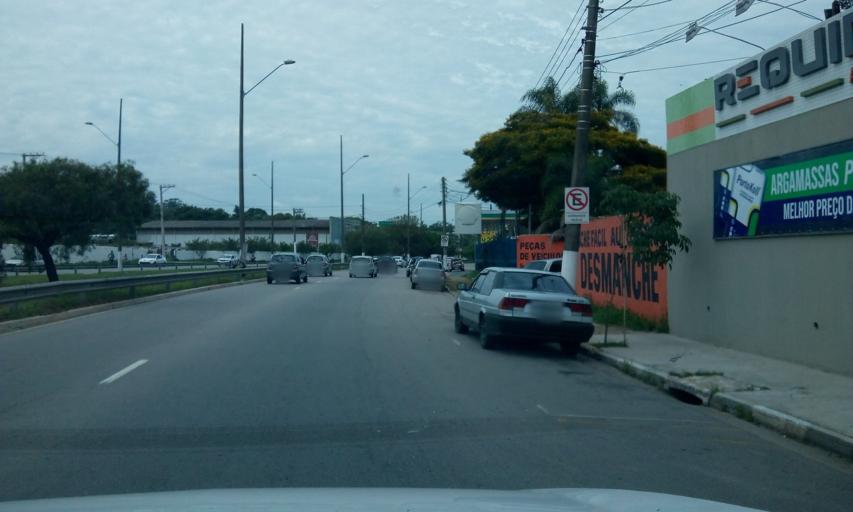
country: BR
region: Sao Paulo
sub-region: Jundiai
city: Jundiai
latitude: -23.2187
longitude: -46.8744
